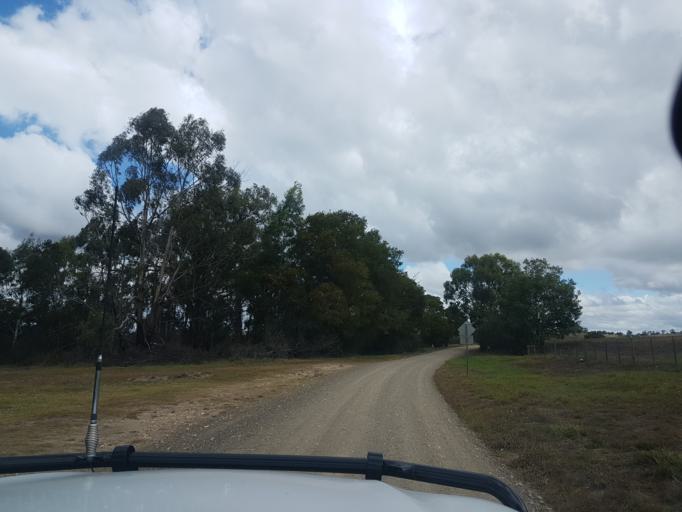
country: AU
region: Victoria
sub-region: East Gippsland
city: Bairnsdale
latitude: -37.7849
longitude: 147.5486
